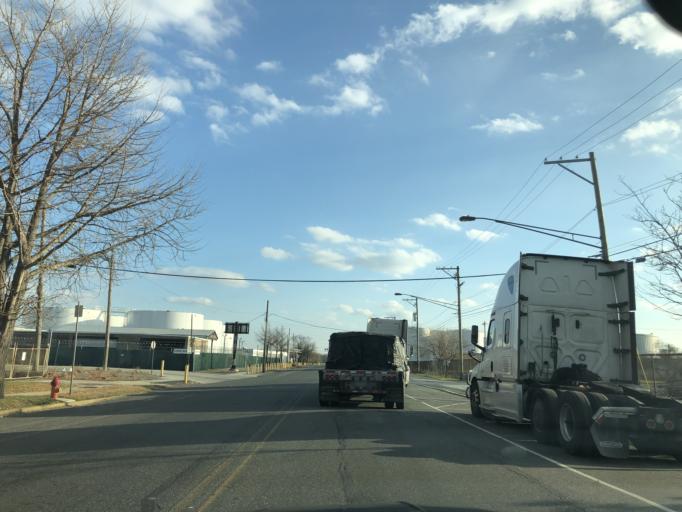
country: US
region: New Jersey
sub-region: Camden County
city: Merchantville
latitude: 39.9806
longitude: -75.0993
